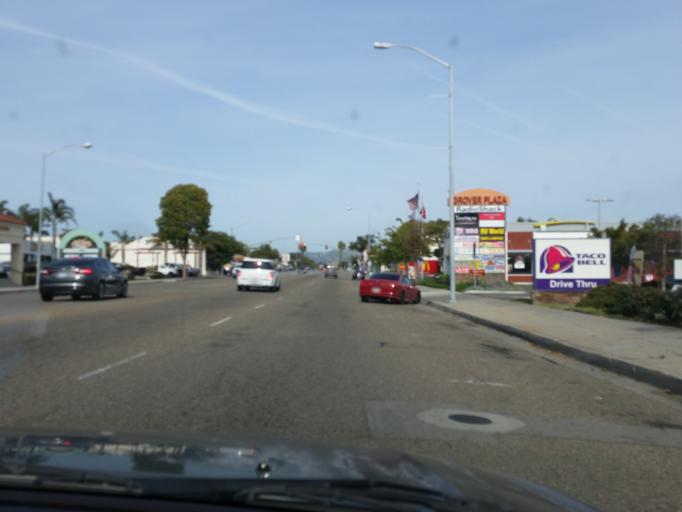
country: US
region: California
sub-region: San Luis Obispo County
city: Grover Beach
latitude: 35.1211
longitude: -120.6134
